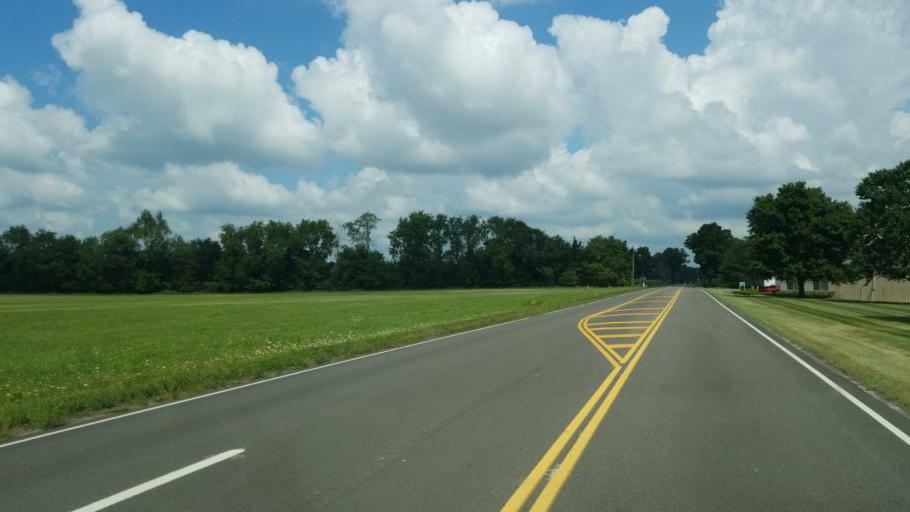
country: US
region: Ohio
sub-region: Knox County
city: Mount Vernon
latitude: 40.3657
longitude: -82.4909
